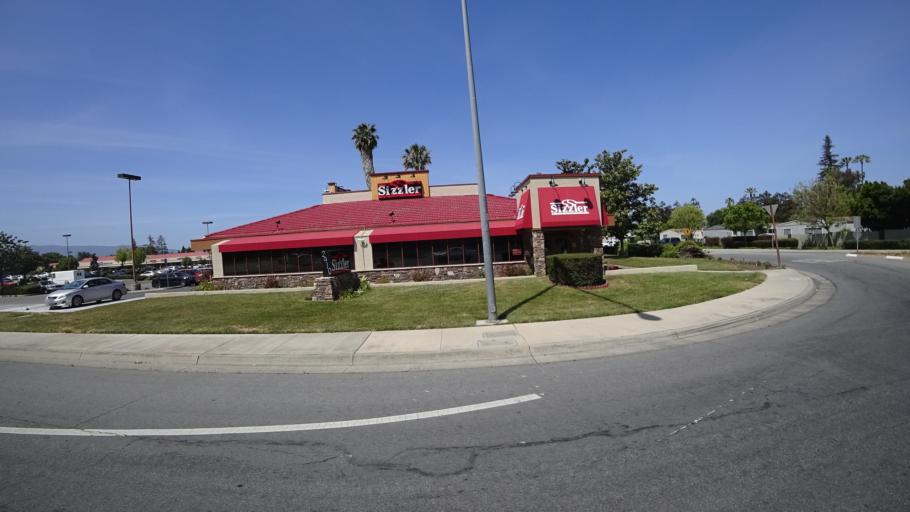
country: US
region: California
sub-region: Santa Clara County
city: Seven Trees
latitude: 37.3137
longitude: -121.8081
